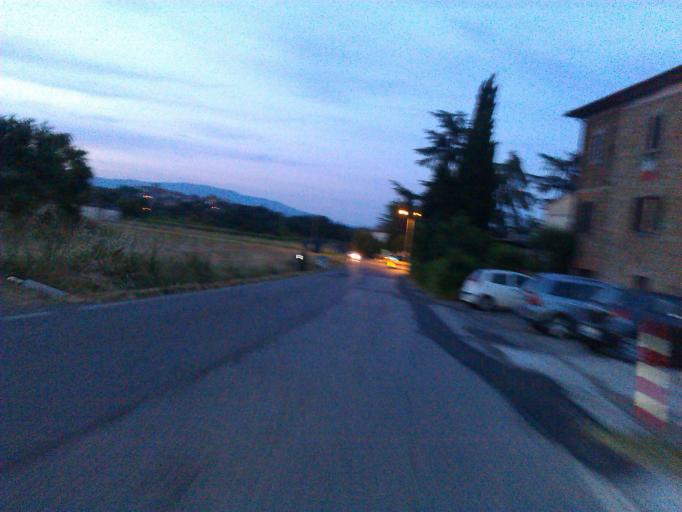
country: IT
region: Tuscany
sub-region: Province of Arezzo
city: Battifolle-Ruscello-Poggiola
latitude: 43.4473
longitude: 11.7958
